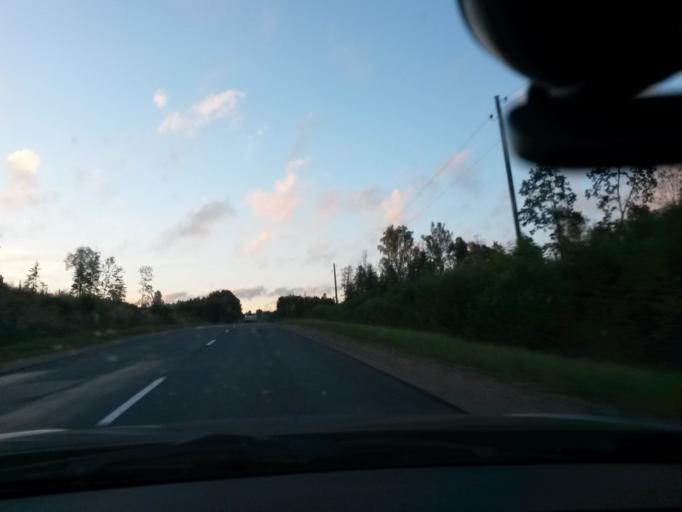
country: LV
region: Madonas Rajons
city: Madona
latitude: 56.7851
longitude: 26.0305
